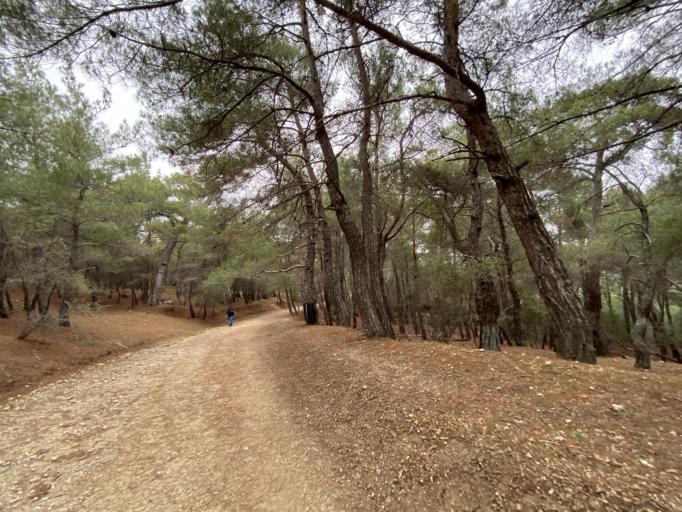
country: TR
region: Canakkale
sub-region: Merkez
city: Kucukkuyu
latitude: 39.5638
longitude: 26.6167
